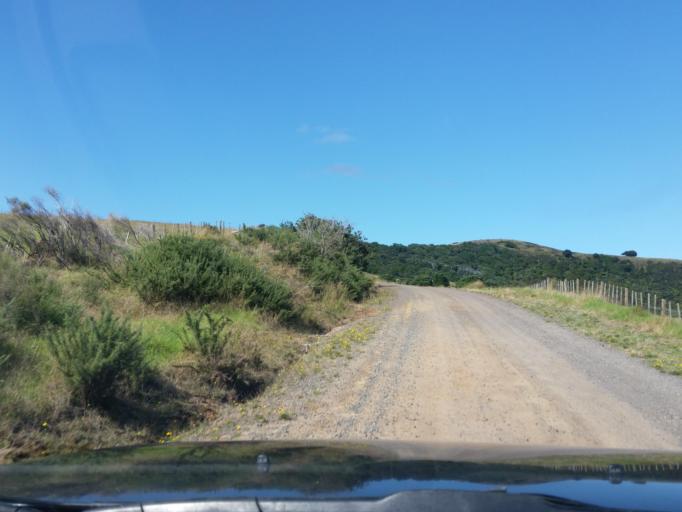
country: NZ
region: Northland
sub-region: Kaipara District
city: Dargaville
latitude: -35.7111
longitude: 173.5401
